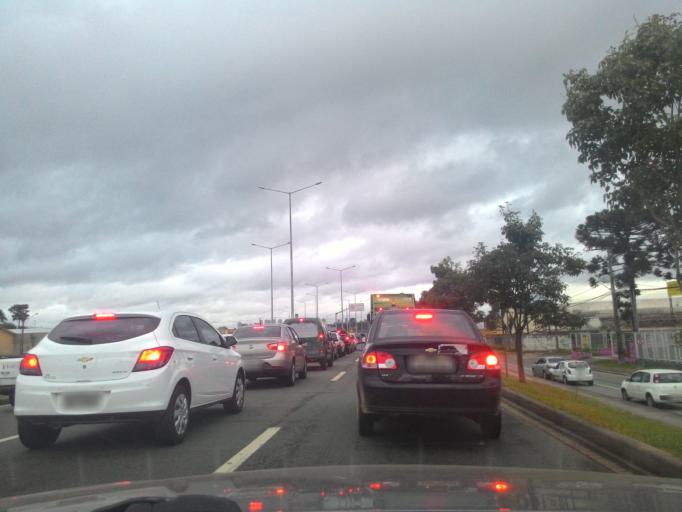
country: BR
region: Parana
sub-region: Curitiba
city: Curitiba
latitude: -25.4781
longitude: -49.2609
